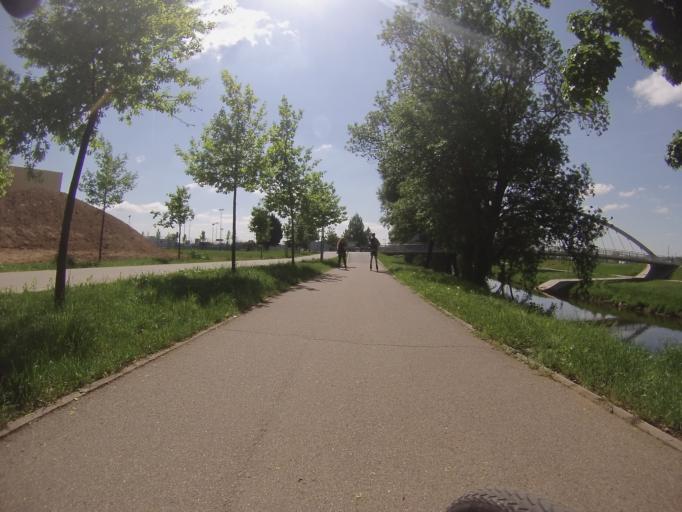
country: CZ
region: South Moravian
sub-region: Mesto Brno
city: Brno
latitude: 49.1699
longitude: 16.6224
